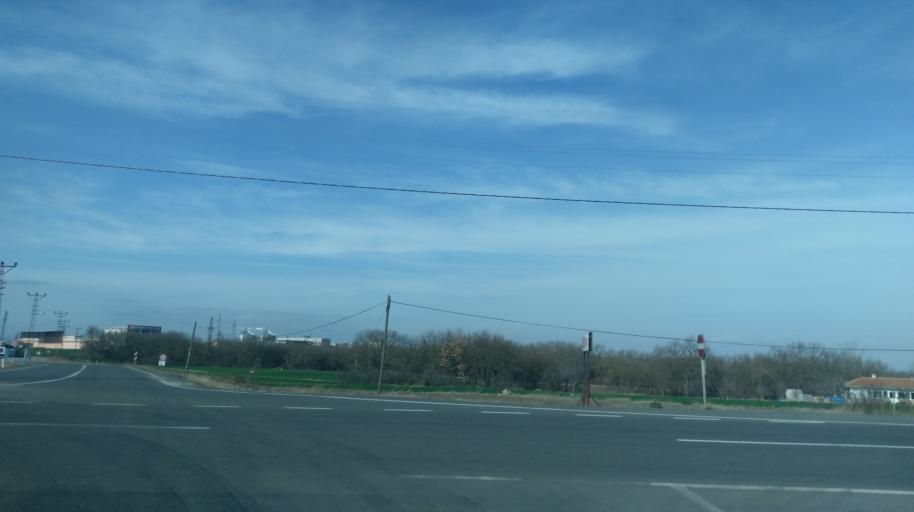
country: TR
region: Edirne
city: Hamidiye
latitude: 41.1519
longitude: 26.6625
